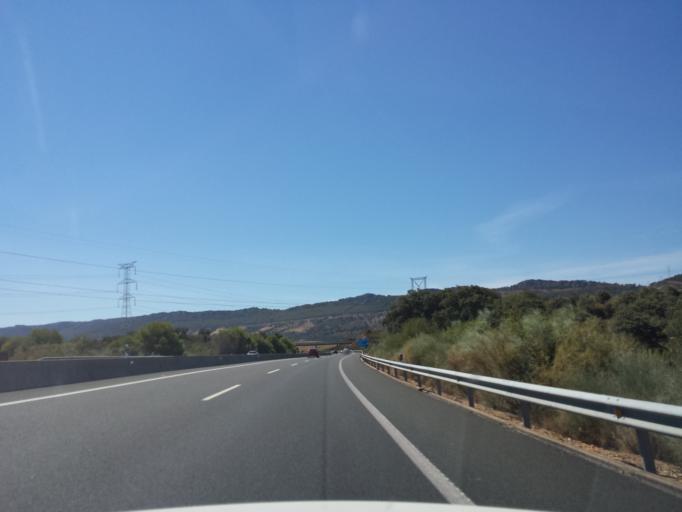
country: ES
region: Extremadura
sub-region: Provincia de Caceres
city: Casas de Miravete
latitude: 39.7413
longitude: -5.7248
